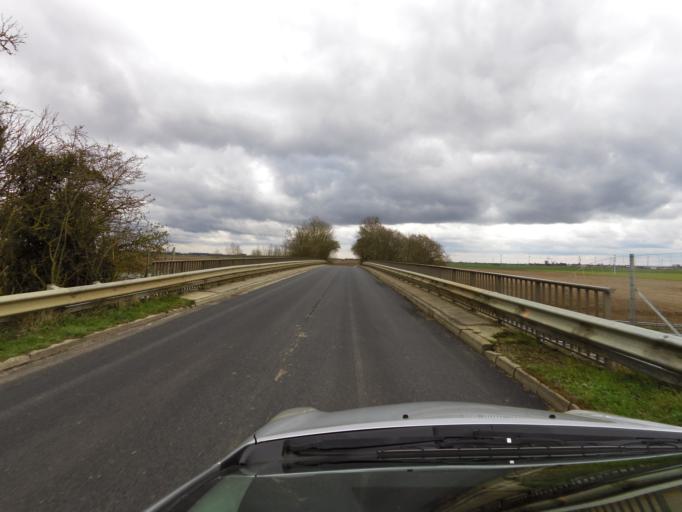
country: FR
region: Picardie
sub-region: Departement de la Somme
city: Roye
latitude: 49.7383
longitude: 2.7848
